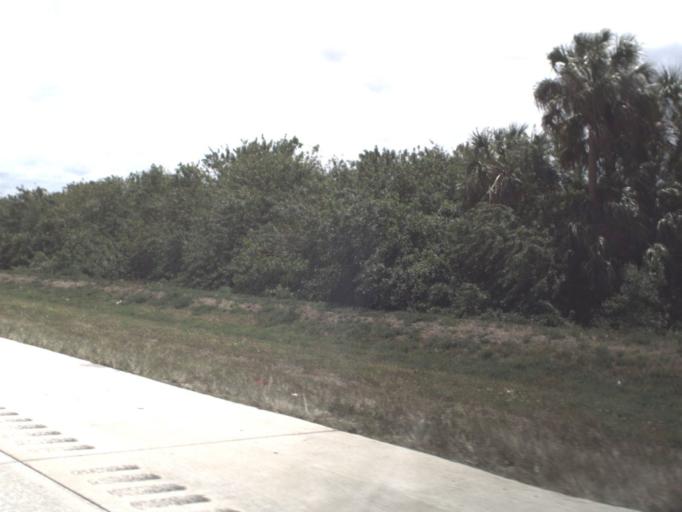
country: US
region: Florida
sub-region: Brevard County
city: Cocoa West
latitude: 28.3469
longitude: -80.7863
